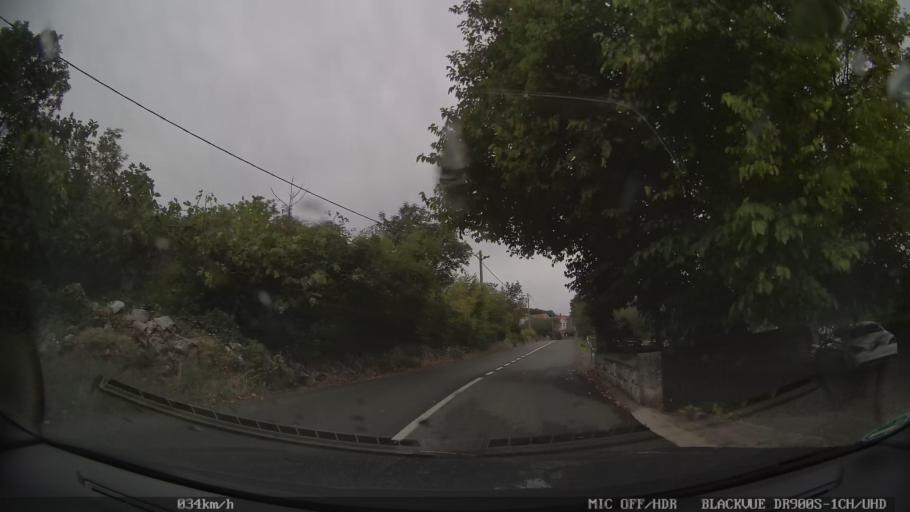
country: HR
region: Primorsko-Goranska
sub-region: Grad Crikvenica
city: Crikvenica
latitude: 45.1053
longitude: 14.6445
